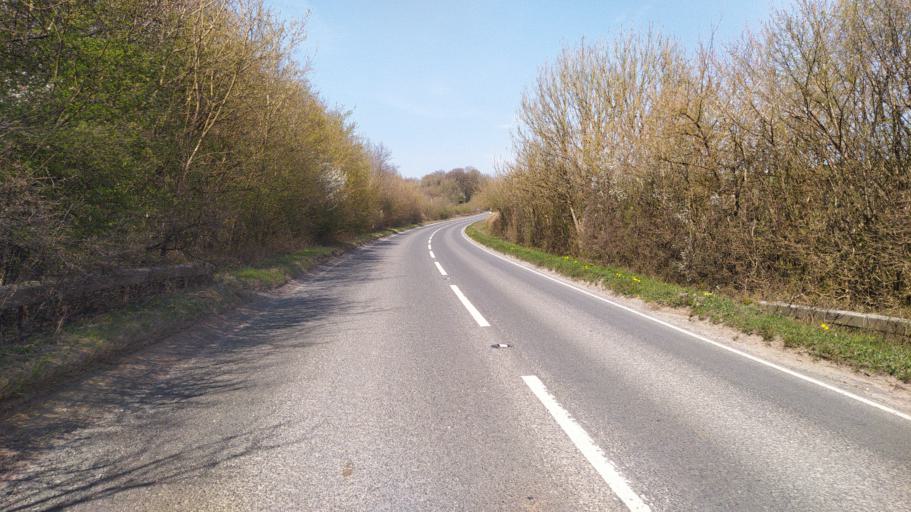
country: GB
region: England
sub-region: Somerset
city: Frome
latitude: 51.2144
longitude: -2.4089
